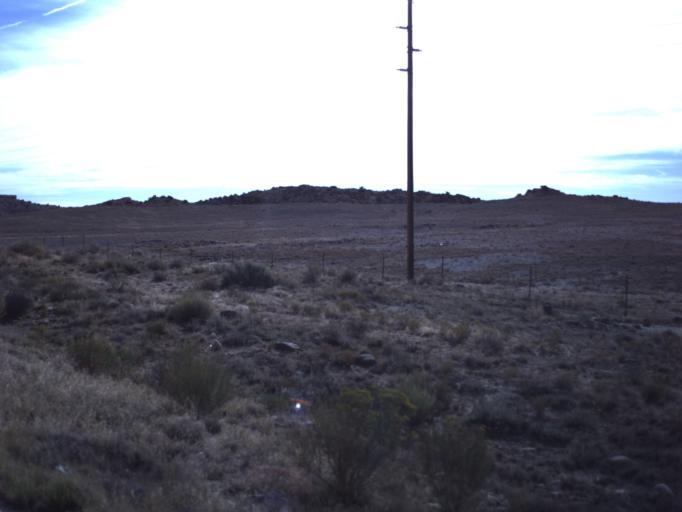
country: US
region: Utah
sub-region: San Juan County
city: Blanding
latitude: 37.4184
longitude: -109.4292
